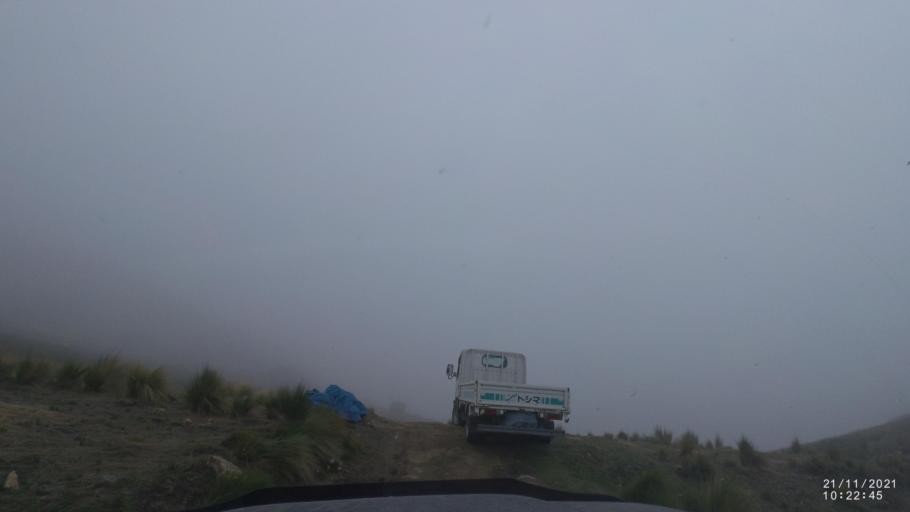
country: BO
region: Cochabamba
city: Cochabamba
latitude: -16.9833
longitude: -66.2612
